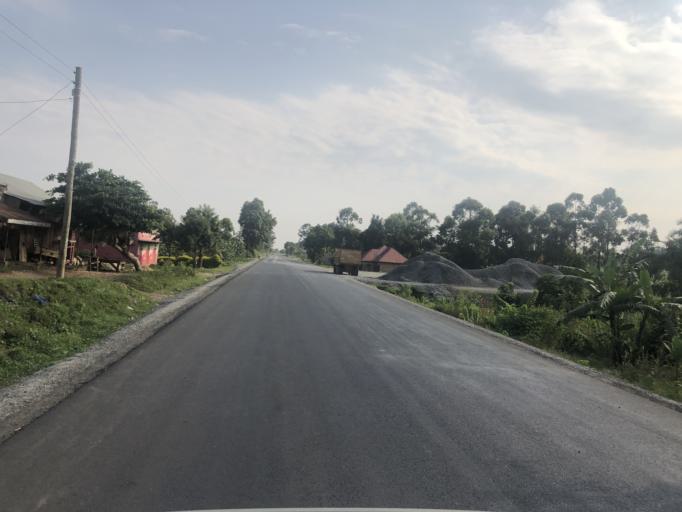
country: UG
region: Western Region
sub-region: Rubirizi District
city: Rubirizi
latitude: -0.2308
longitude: 30.0941
